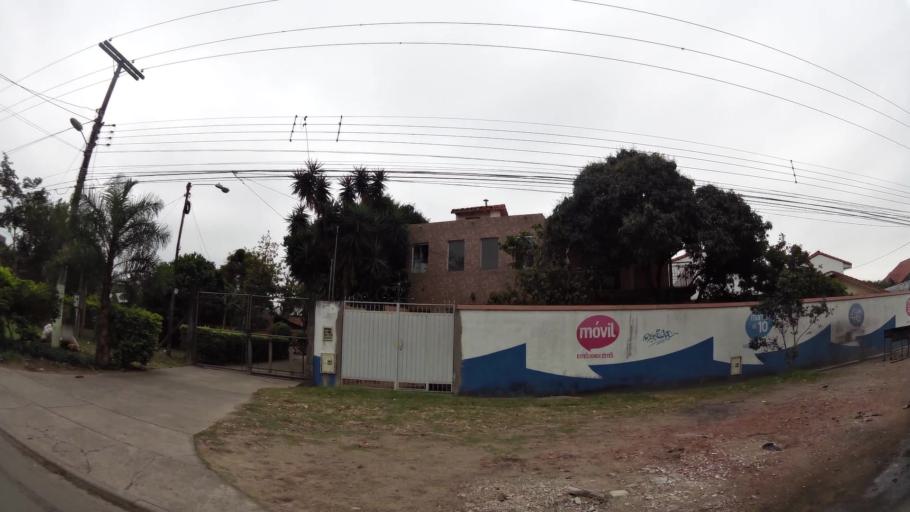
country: BO
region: Santa Cruz
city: Santa Cruz de la Sierra
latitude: -17.7601
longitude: -63.1904
